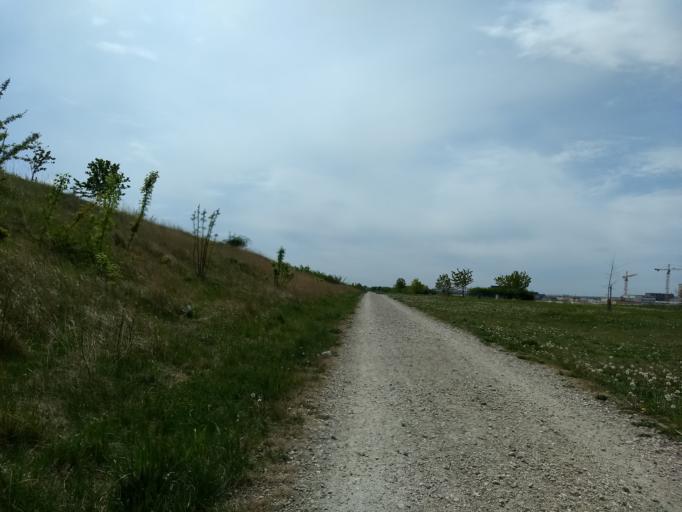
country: AT
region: Lower Austria
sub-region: Politischer Bezirk Ganserndorf
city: Gross-Enzersdorf
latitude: 48.2311
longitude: 16.5165
